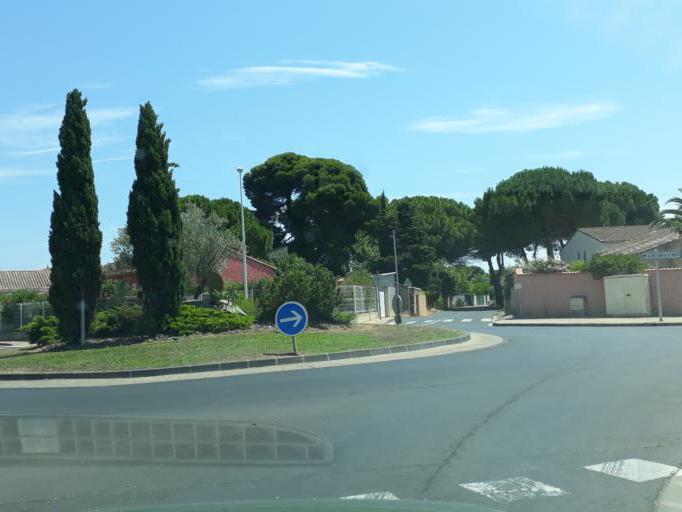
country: FR
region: Languedoc-Roussillon
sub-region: Departement de l'Herault
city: Agde
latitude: 43.2916
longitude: 3.4559
